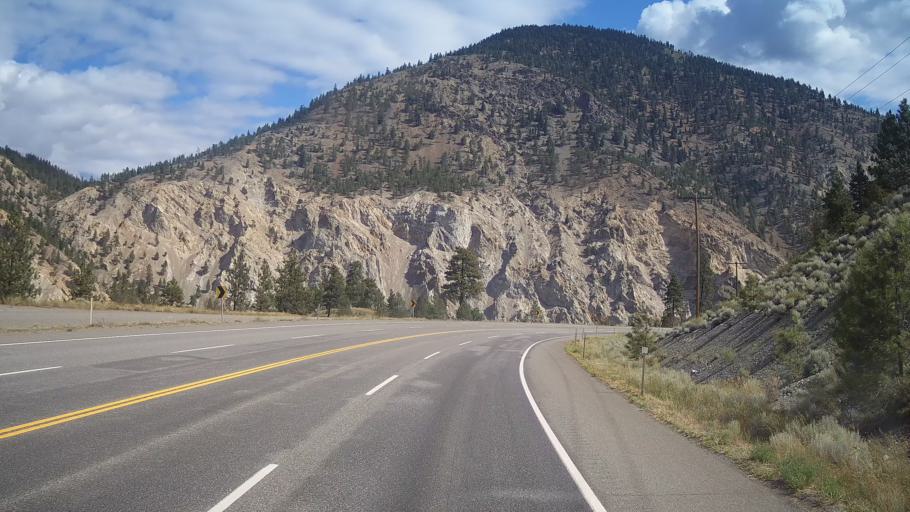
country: CA
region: British Columbia
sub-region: Thompson-Nicola Regional District
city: Ashcroft
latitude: 50.2583
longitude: -121.5408
